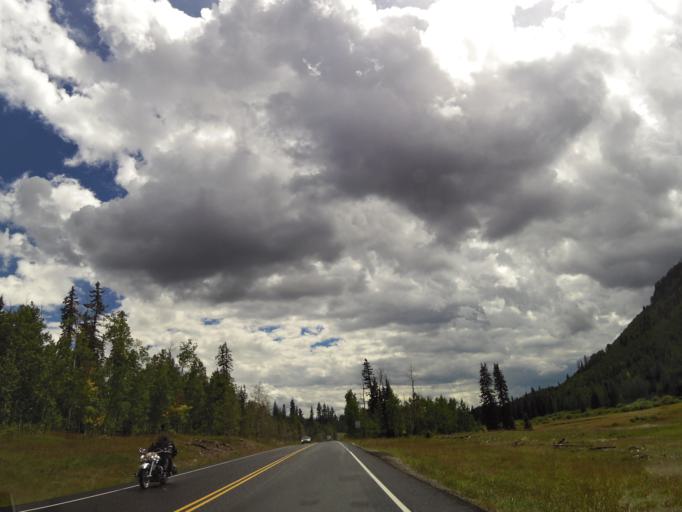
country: US
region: Colorado
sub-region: San Juan County
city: Silverton
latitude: 37.6500
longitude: -107.8083
